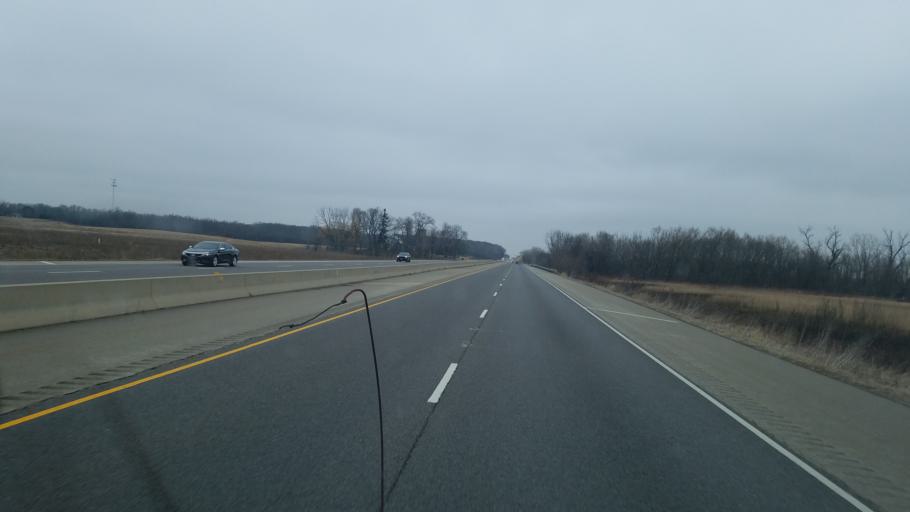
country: US
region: Illinois
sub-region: Lake County
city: Wadsworth
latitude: 42.4160
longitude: -87.9379
